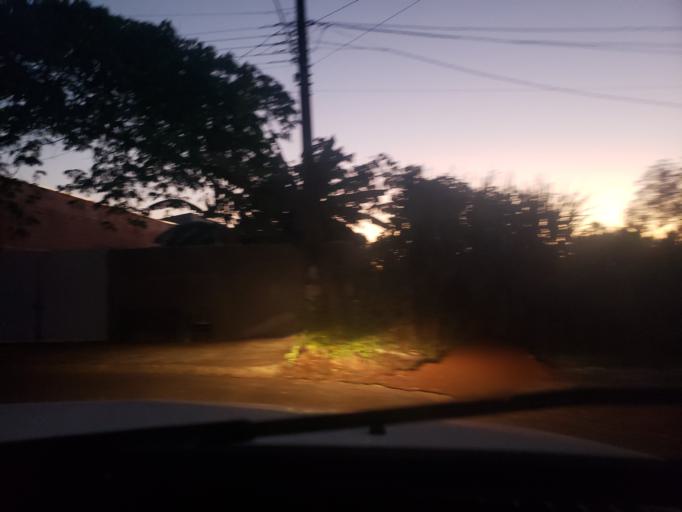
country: BR
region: Sao Paulo
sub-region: Conchal
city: Conchal
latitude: -22.2909
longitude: -47.1322
